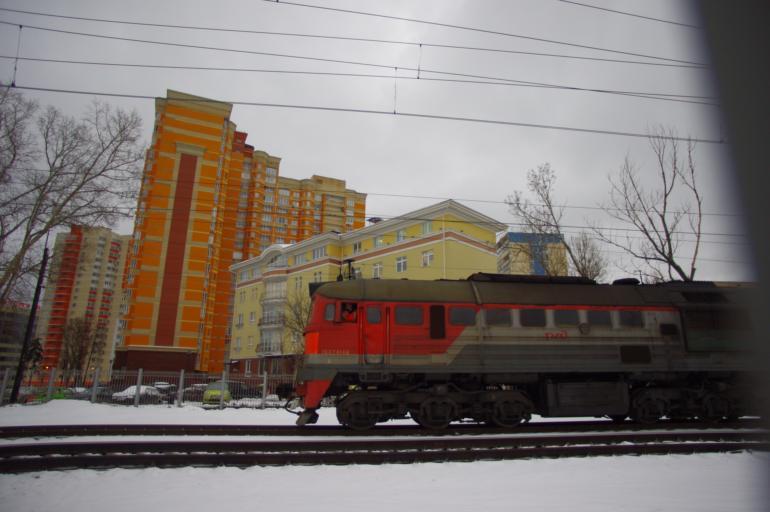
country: RU
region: Moskovskaya
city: Pavshino
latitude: 55.8167
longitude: 37.3493
